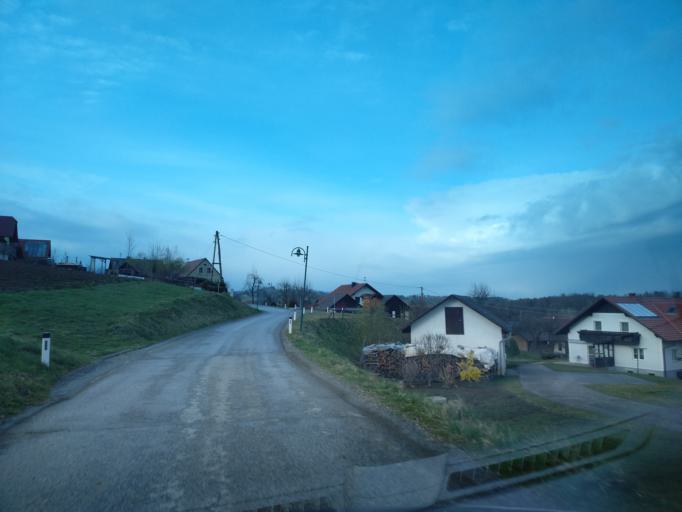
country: AT
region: Styria
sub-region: Politischer Bezirk Deutschlandsberg
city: Pitschgau
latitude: 46.6852
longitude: 15.2644
